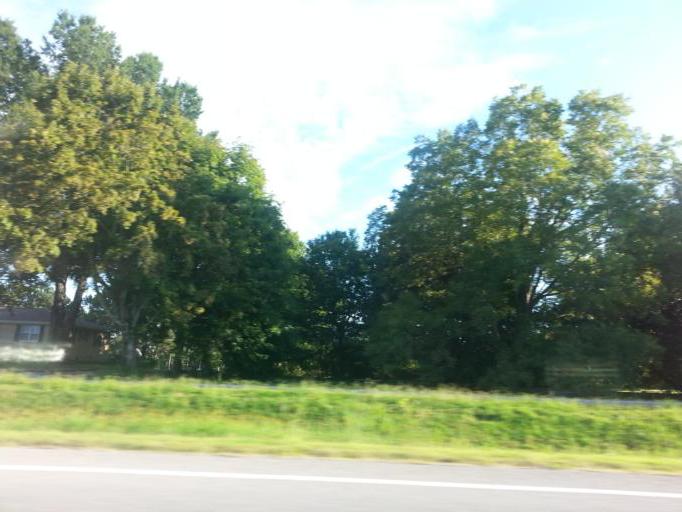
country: US
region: Alabama
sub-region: Lauderdale County
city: Killen
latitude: 34.8598
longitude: -87.4411
